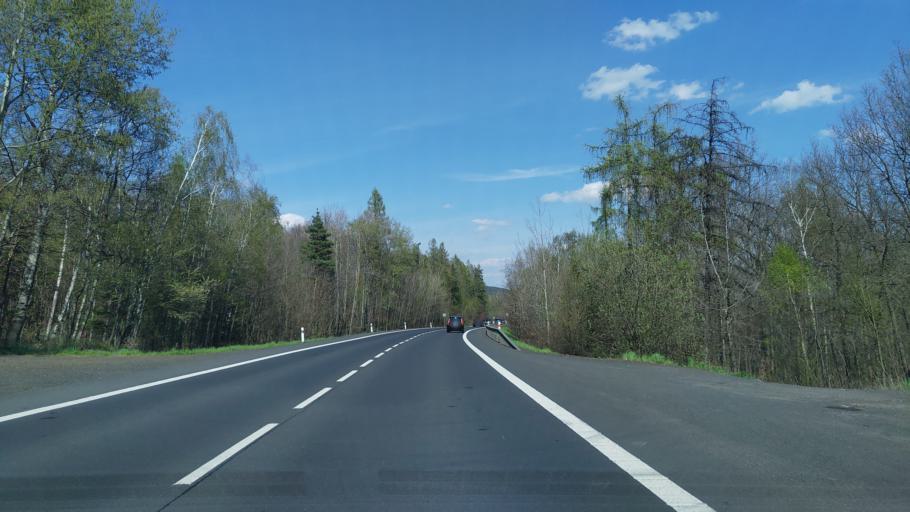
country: CZ
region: Ustecky
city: Kadan
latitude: 50.4361
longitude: 13.2901
